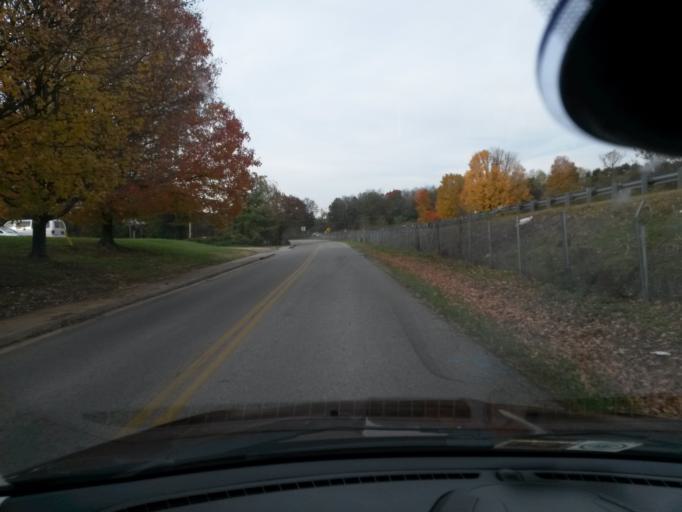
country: US
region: Virginia
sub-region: Roanoke County
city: Hollins
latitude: 37.3090
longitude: -79.9765
